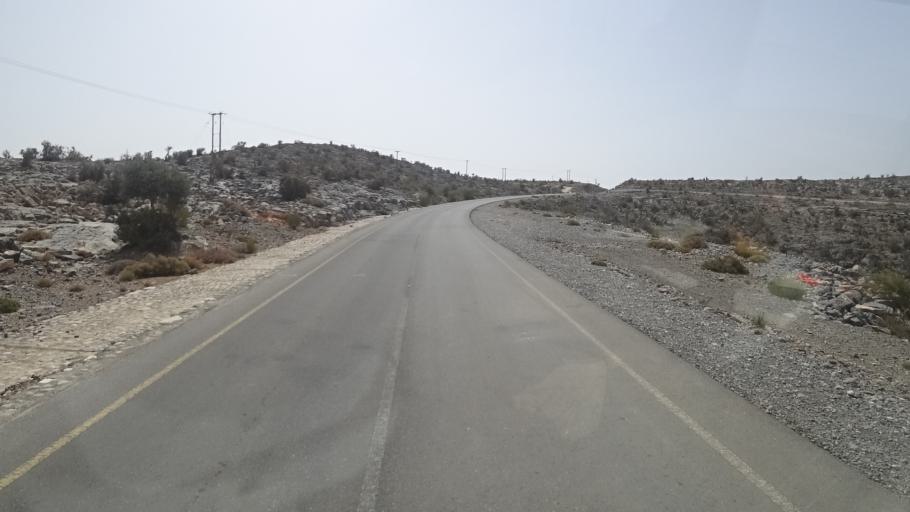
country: OM
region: Al Batinah
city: Bayt al `Awabi
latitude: 23.1496
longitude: 57.4229
